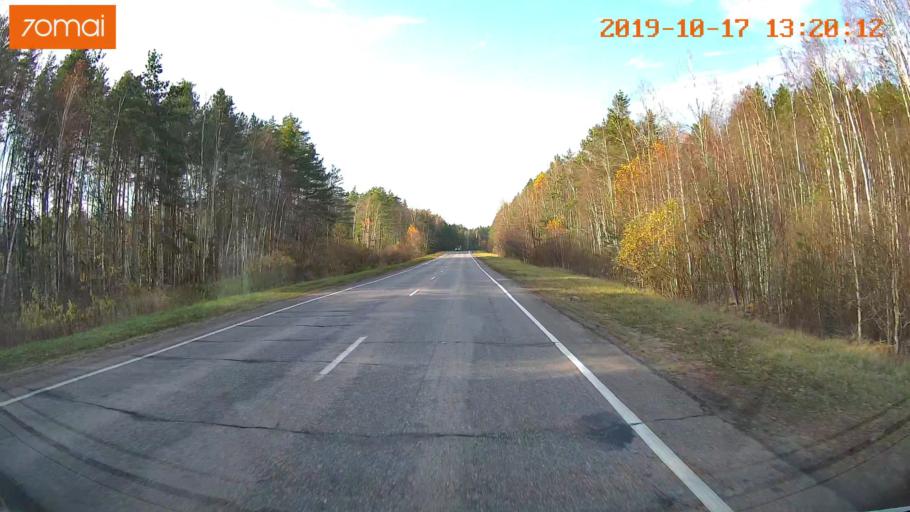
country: RU
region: Rjazan
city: Gus'-Zheleznyy
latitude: 55.0744
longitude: 41.0557
